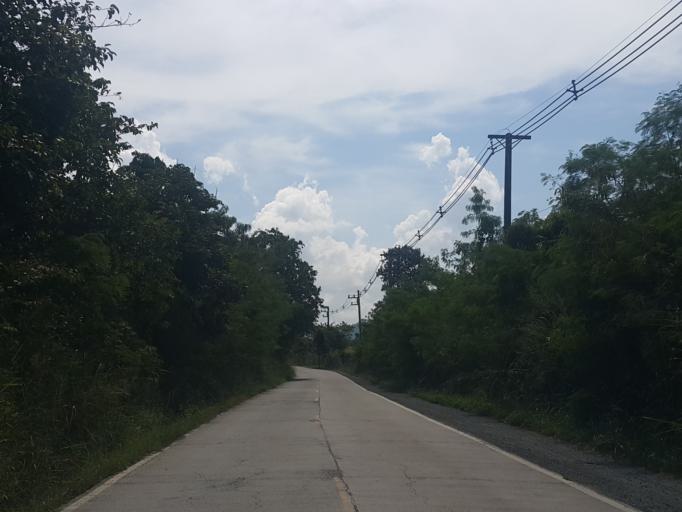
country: TH
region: Chiang Mai
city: Mae On
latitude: 18.8228
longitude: 99.2170
